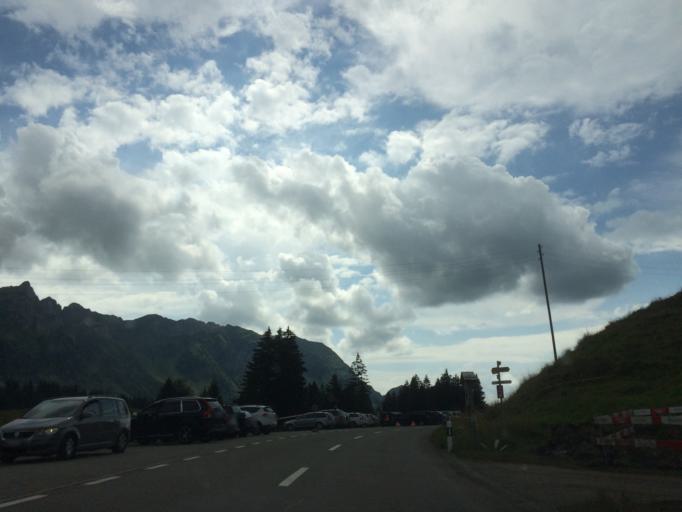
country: CH
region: Appenzell Ausserrhoden
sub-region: Bezirk Hinterland
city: Urnasch
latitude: 47.2545
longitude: 9.3053
